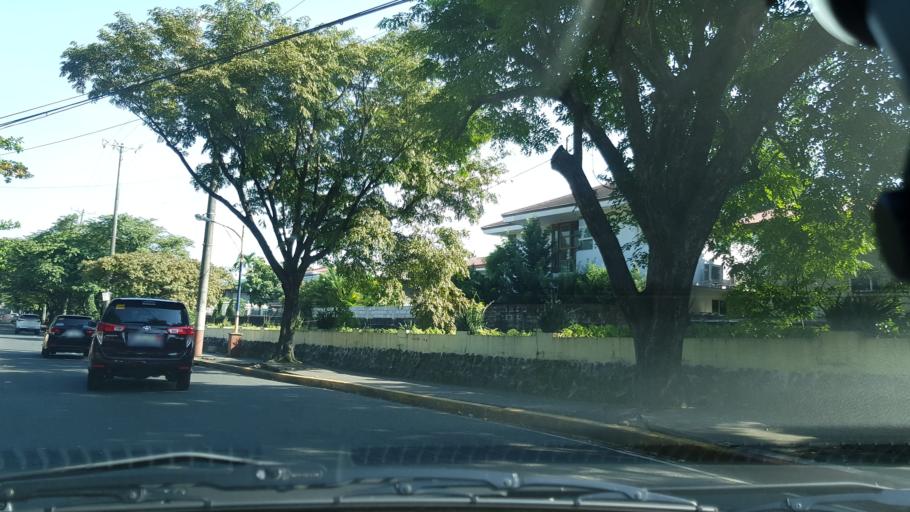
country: PH
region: Metro Manila
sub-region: Pasig
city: Pasig City
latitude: 14.5795
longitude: 121.0712
